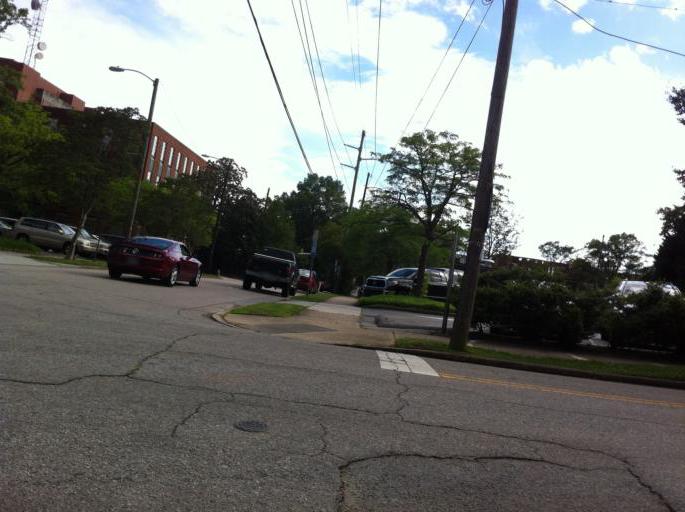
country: US
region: North Carolina
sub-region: Wake County
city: West Raleigh
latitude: 35.7895
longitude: -78.6708
